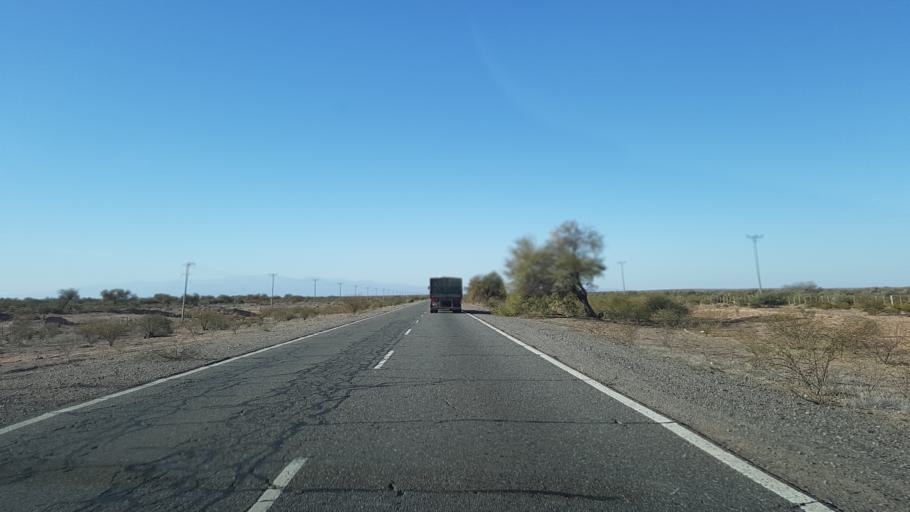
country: AR
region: San Juan
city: Caucete
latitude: -31.6552
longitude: -67.7701
